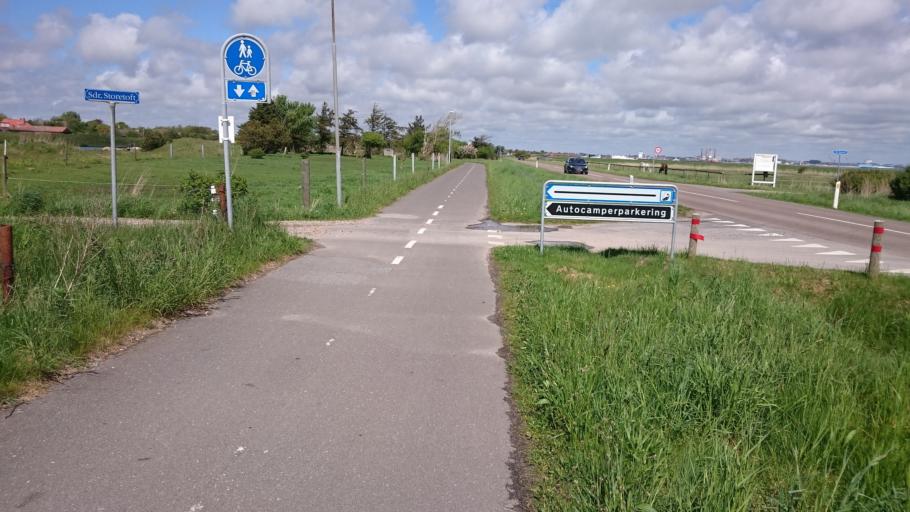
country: DK
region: South Denmark
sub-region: Fano Kommune
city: Nordby
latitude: 55.4336
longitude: 8.3944
